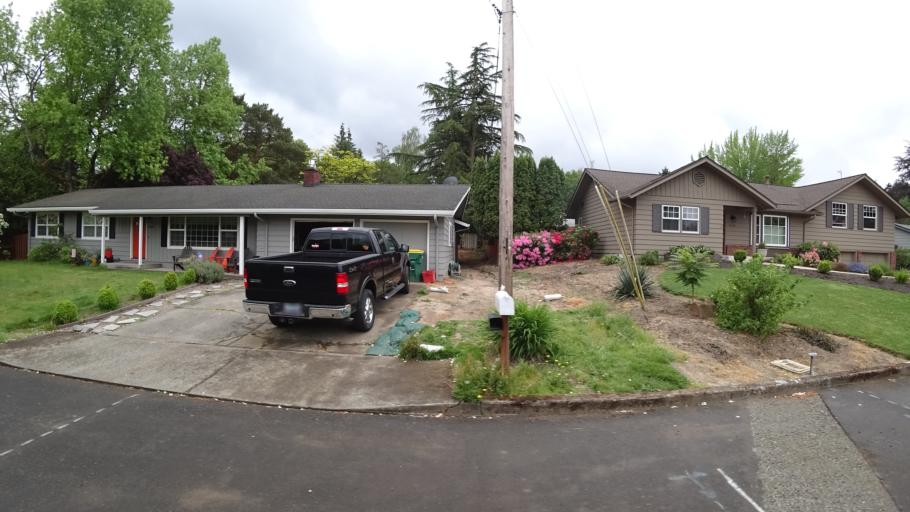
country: US
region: Oregon
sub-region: Washington County
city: Garden Home-Whitford
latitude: 45.4645
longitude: -122.7722
